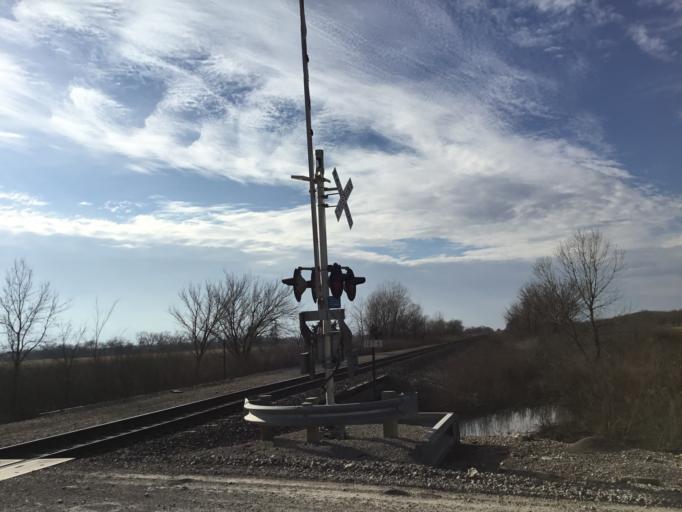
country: US
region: Kansas
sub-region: Chase County
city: Cottonwood Falls
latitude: 38.3876
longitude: -96.4649
